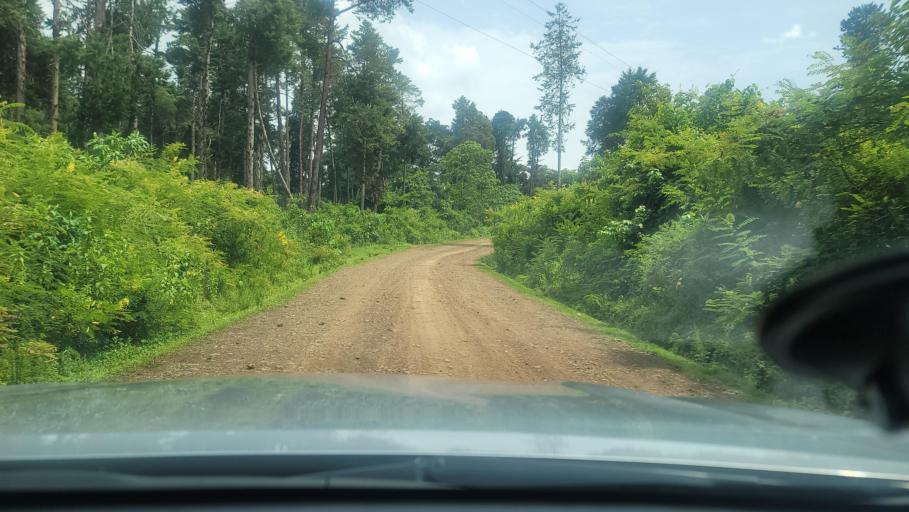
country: ET
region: Oromiya
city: Agaro
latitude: 7.7935
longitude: 36.4177
